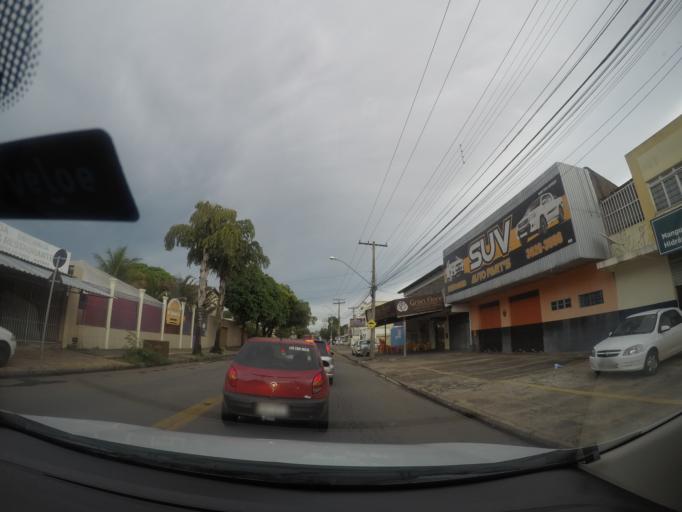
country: BR
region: Goias
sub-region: Goiania
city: Goiania
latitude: -16.7068
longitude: -49.3073
